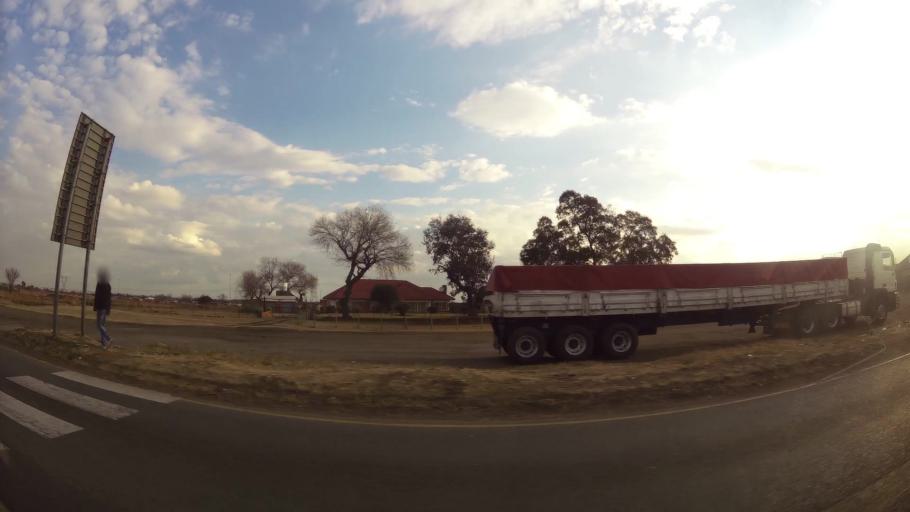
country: ZA
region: Gauteng
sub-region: Sedibeng District Municipality
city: Vanderbijlpark
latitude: -26.6950
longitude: 27.8065
